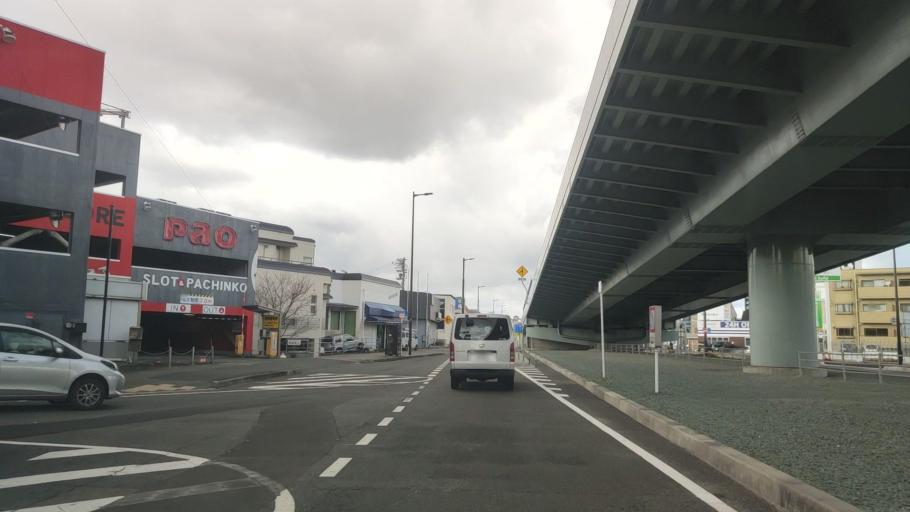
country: JP
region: Ehime
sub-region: Shikoku-chuo Shi
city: Matsuyama
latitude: 33.8270
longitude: 132.7828
